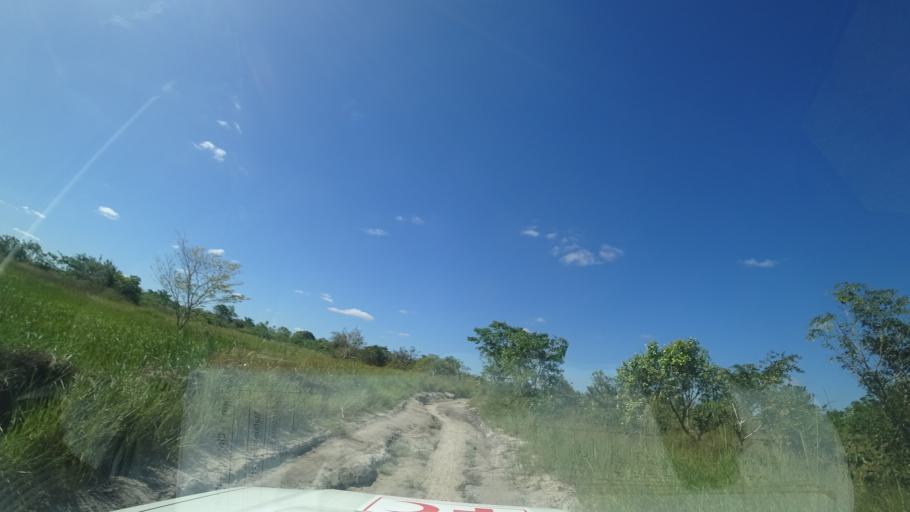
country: MZ
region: Sofala
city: Dondo
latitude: -19.4775
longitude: 34.6273
